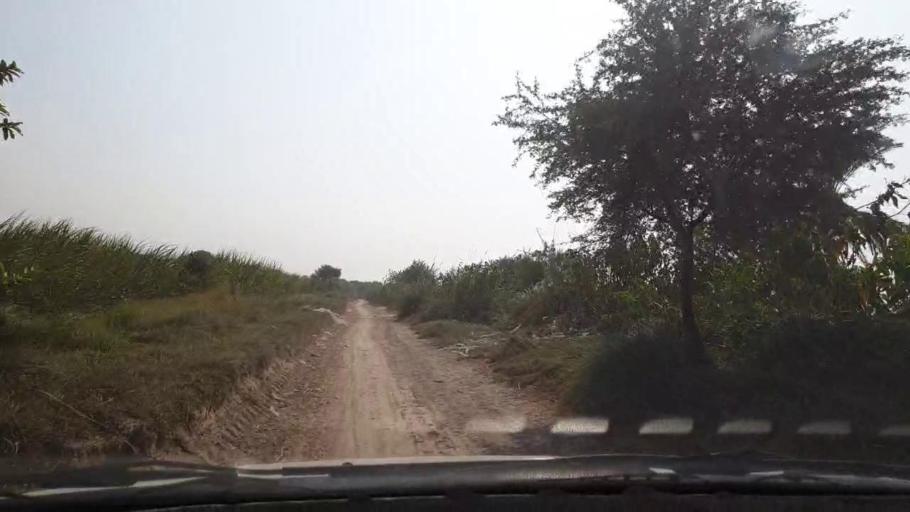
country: PK
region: Sindh
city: Tando Muhammad Khan
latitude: 25.0828
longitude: 68.3601
